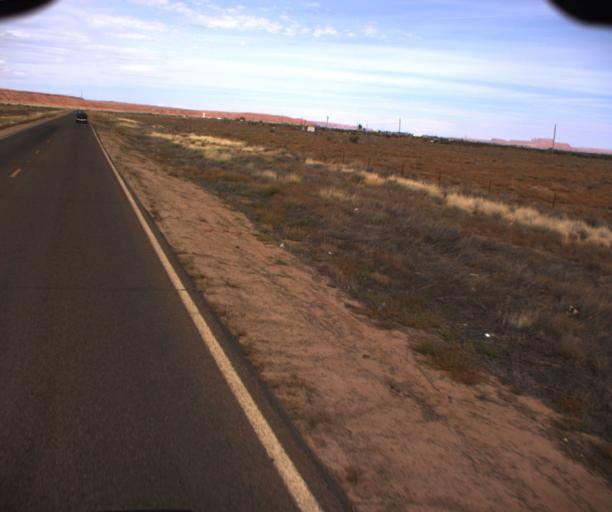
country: US
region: Arizona
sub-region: Apache County
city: Many Farms
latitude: 36.3269
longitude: -109.6198
